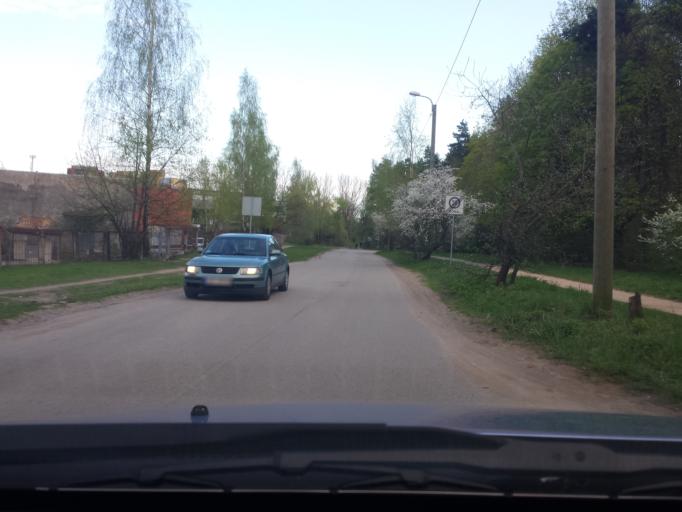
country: LV
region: Riga
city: Jaunciems
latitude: 56.9953
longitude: 24.2261
